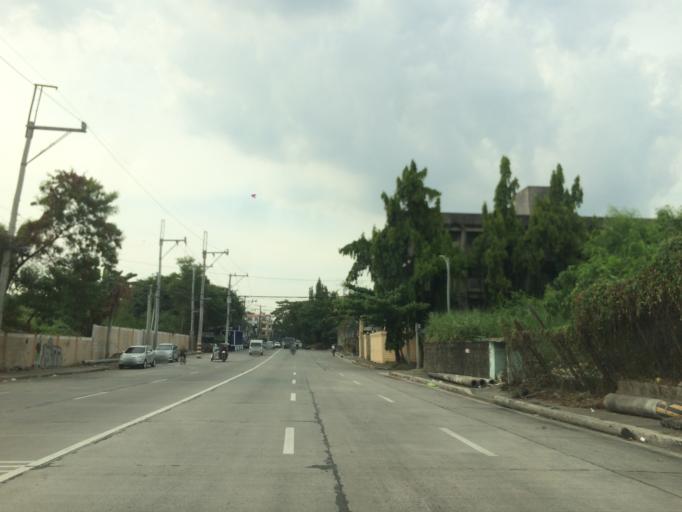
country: PH
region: Calabarzon
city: Del Monte
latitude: 14.6324
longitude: 121.0072
